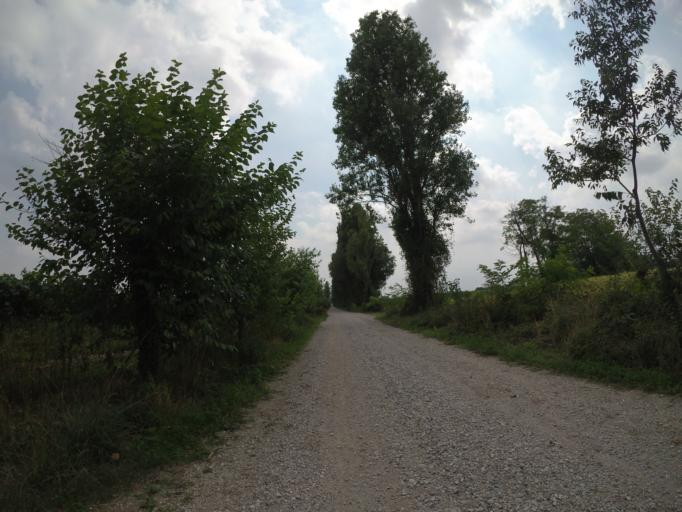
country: IT
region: Friuli Venezia Giulia
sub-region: Provincia di Udine
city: Sedegliano
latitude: 46.0074
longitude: 13.0107
